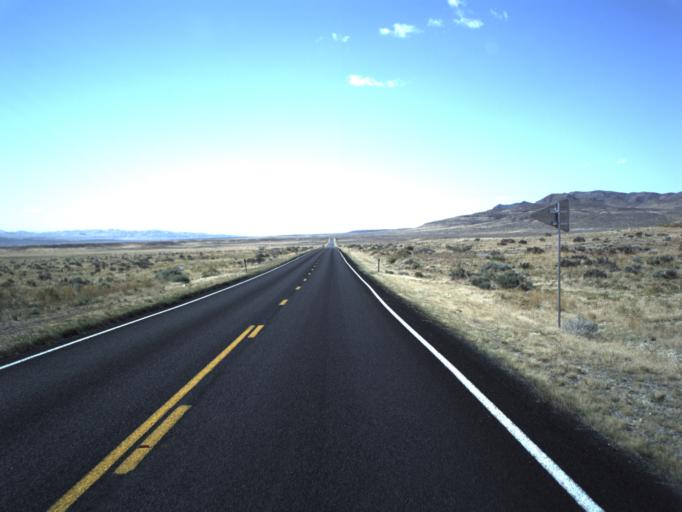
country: US
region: Utah
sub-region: Millard County
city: Fillmore
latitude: 38.9066
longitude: -112.8189
